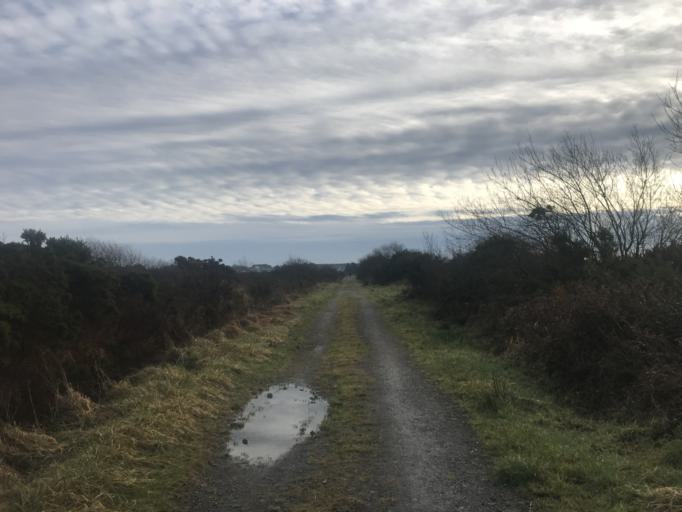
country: IE
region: Connaught
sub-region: County Galway
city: Gaillimh
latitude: 53.3214
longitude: -9.0100
